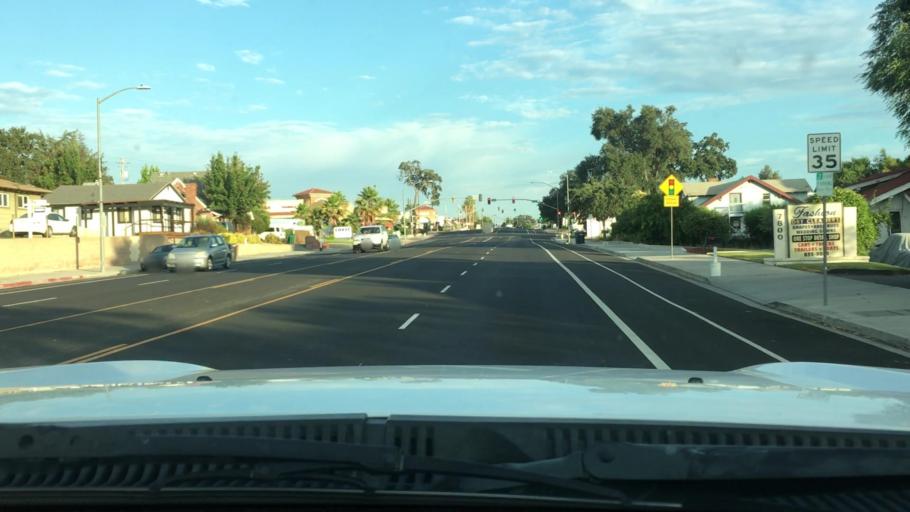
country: US
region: California
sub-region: San Luis Obispo County
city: Atascadero
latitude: 35.4788
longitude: -120.6572
